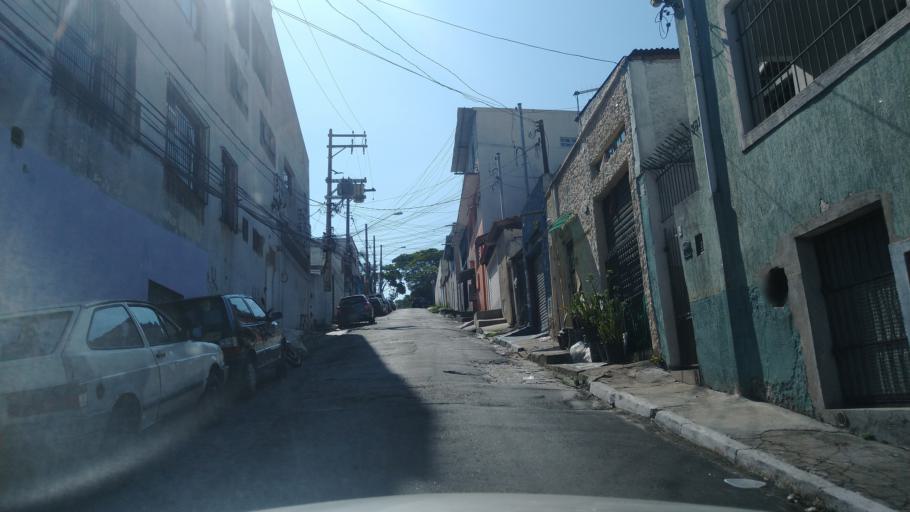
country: BR
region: Sao Paulo
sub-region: Sao Paulo
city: Sao Paulo
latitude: -23.4801
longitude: -46.6218
